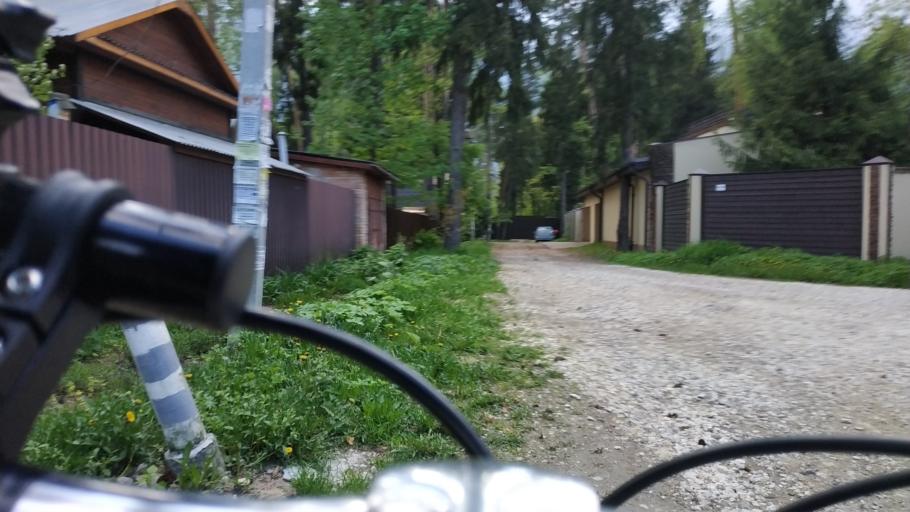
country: RU
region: Moskovskaya
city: Kratovo
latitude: 55.6027
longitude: 38.1562
